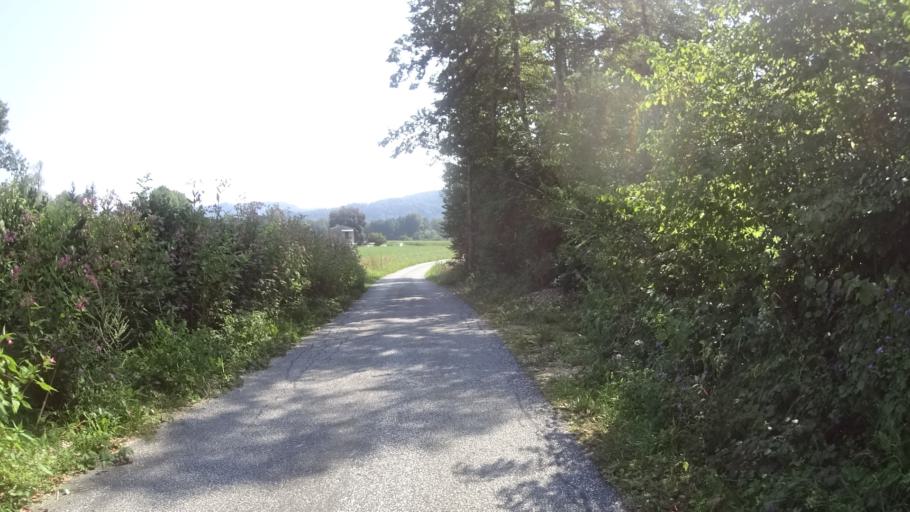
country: AT
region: Carinthia
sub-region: Politischer Bezirk Volkermarkt
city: Gallizien
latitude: 46.5600
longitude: 14.4894
